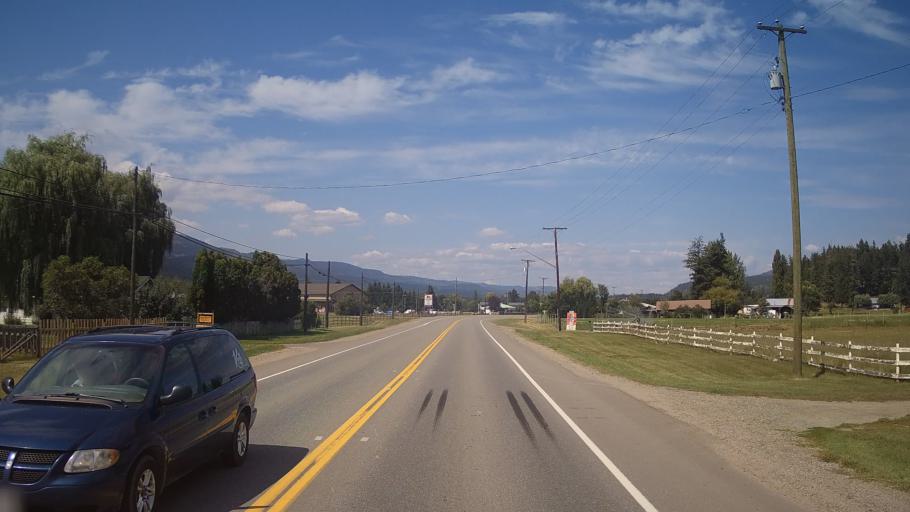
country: CA
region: British Columbia
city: Kamloops
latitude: 51.1661
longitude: -120.1250
